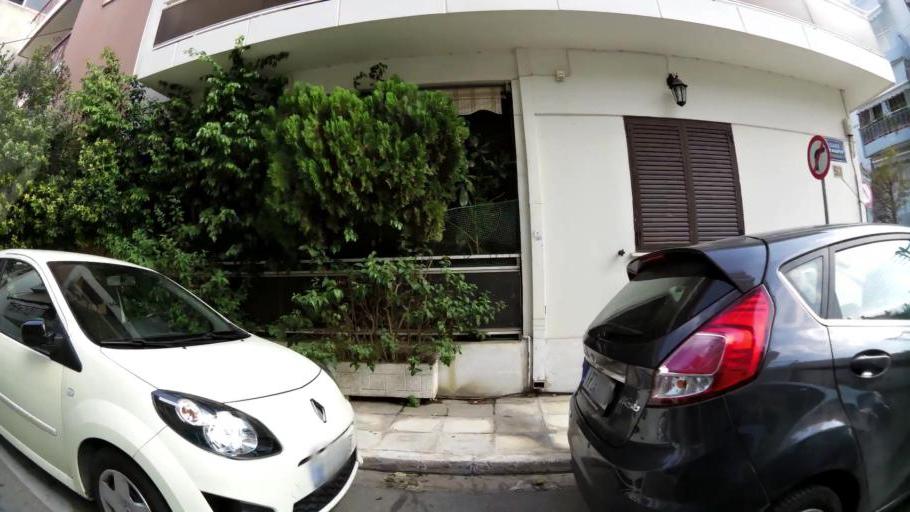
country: GR
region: Attica
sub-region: Nomarchia Athinas
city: Ilion
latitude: 38.0374
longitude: 23.6981
